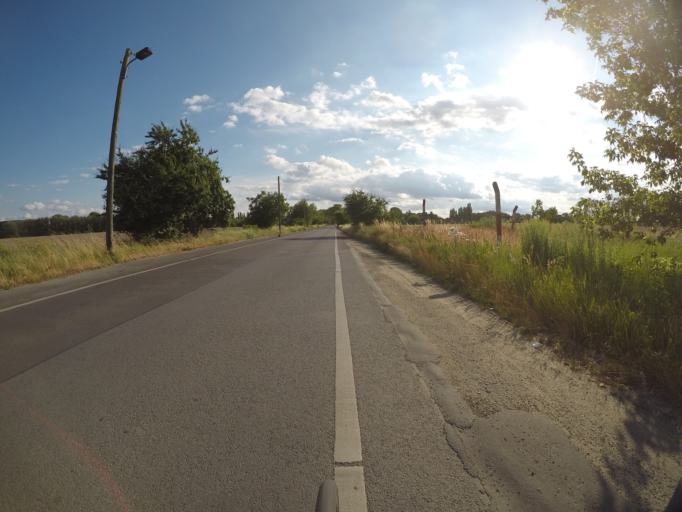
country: DE
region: Berlin
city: Wartenberg
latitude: 52.5816
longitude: 13.5259
